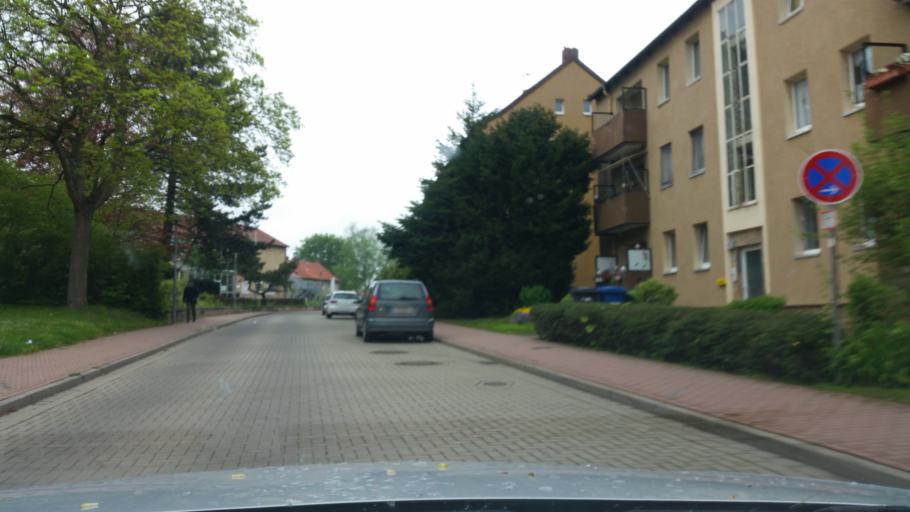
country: DE
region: Lower Saxony
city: Schoningen
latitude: 52.1430
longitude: 10.9657
